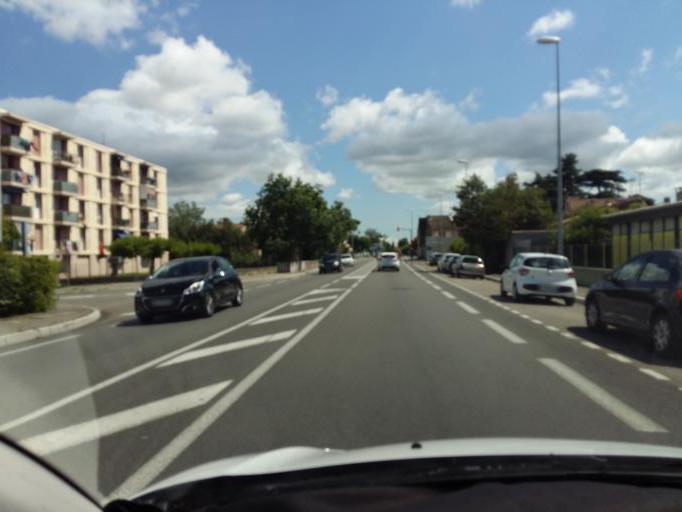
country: FR
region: Provence-Alpes-Cote d'Azur
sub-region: Departement du Vaucluse
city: Cavaillon
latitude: 43.8400
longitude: 5.0478
